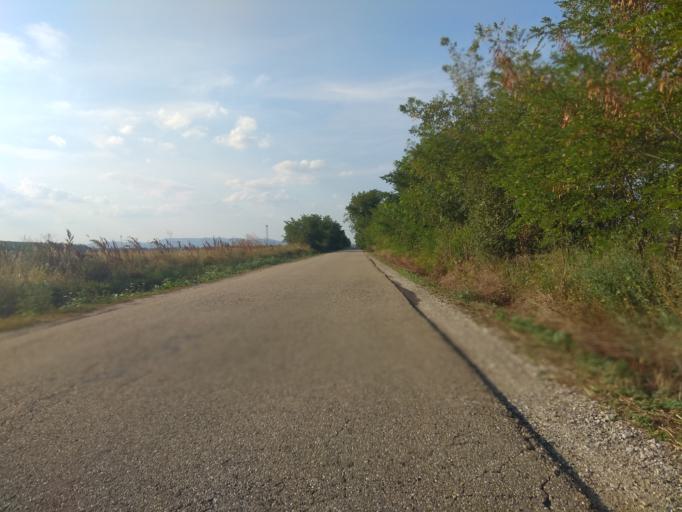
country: HU
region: Borsod-Abauj-Zemplen
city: Harsany
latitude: 47.9093
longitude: 20.7427
